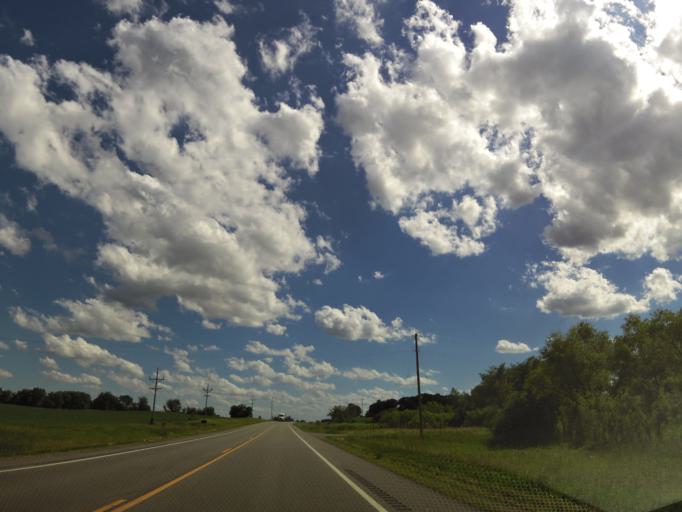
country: US
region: Minnesota
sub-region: Stearns County
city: Rockville
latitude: 45.3009
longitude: -94.3026
